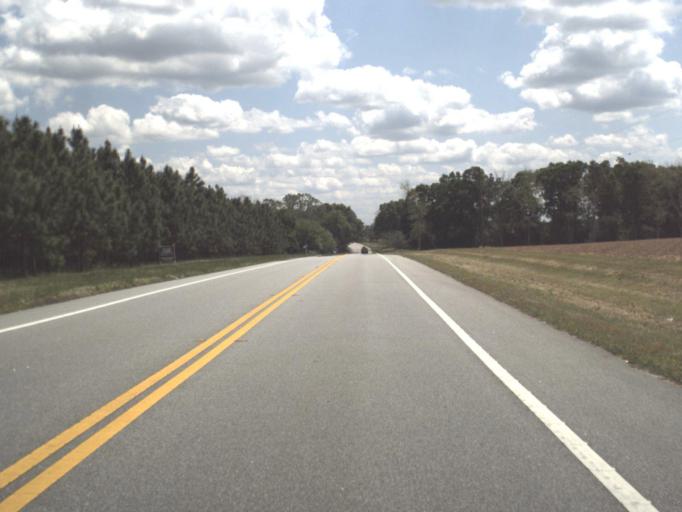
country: US
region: Alabama
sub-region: Escambia County
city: Atmore
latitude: 30.8801
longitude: -87.4467
